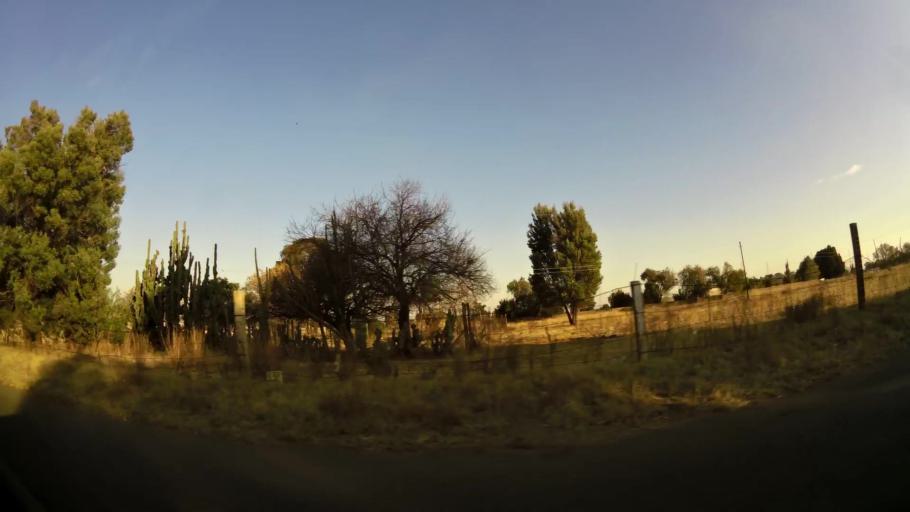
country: ZA
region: Gauteng
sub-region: West Rand District Municipality
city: Randfontein
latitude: -26.2020
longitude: 27.6462
